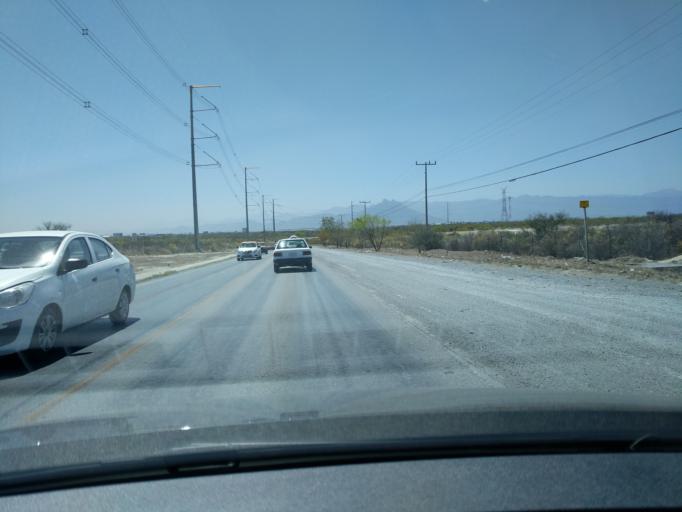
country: MX
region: Nuevo Leon
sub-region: Apodaca
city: Artemio Trevino
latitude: 25.8239
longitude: -100.1440
